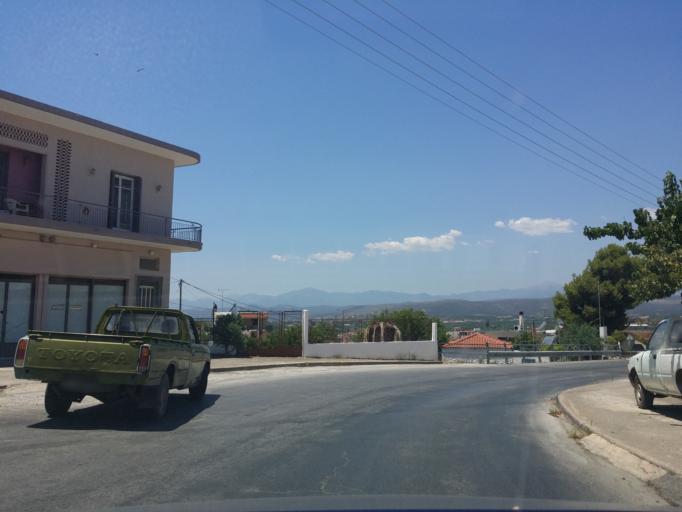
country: GR
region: Peloponnese
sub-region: Nomos Lakonias
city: Vlakhiotis
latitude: 36.8618
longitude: 22.7135
